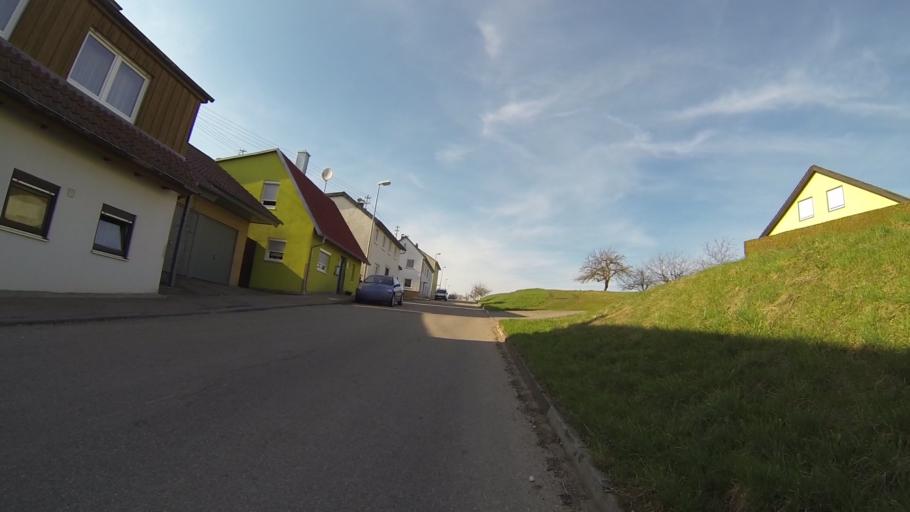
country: DE
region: Baden-Wuerttemberg
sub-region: Regierungsbezirk Stuttgart
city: Niederstotzingen
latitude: 48.5433
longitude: 10.2348
